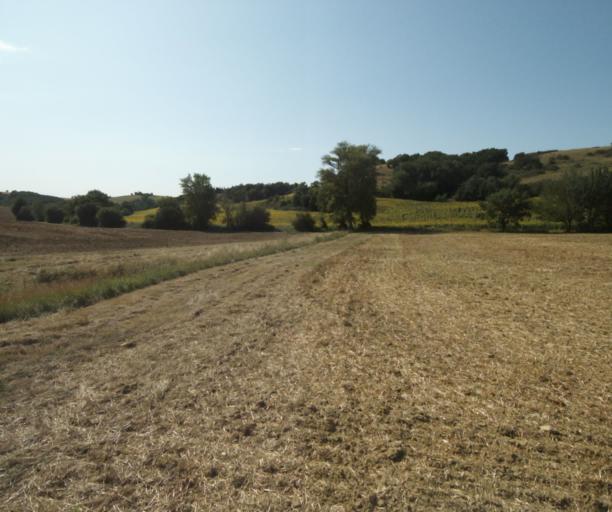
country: FR
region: Midi-Pyrenees
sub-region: Departement de la Haute-Garonne
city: Saint-Felix-Lauragais
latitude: 43.4192
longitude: 1.8346
